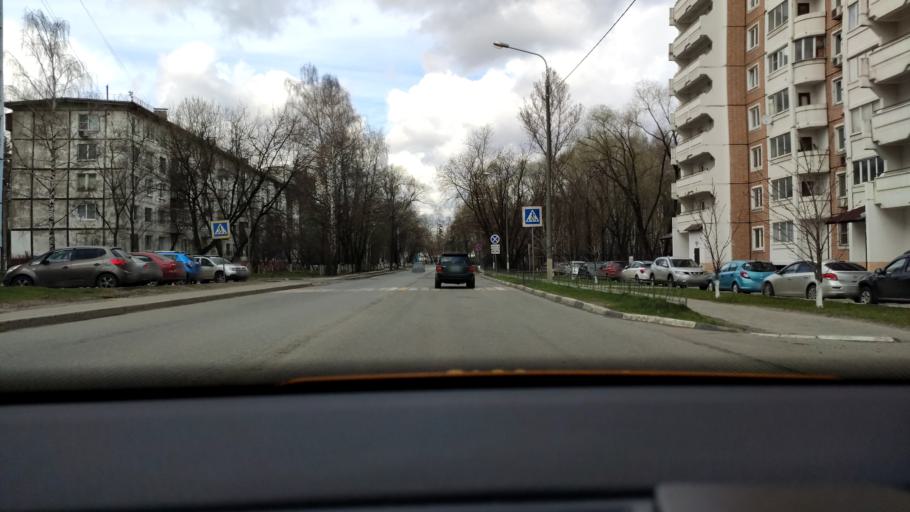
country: RU
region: Moskovskaya
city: Zheleznodorozhnyy
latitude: 55.7447
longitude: 38.0351
